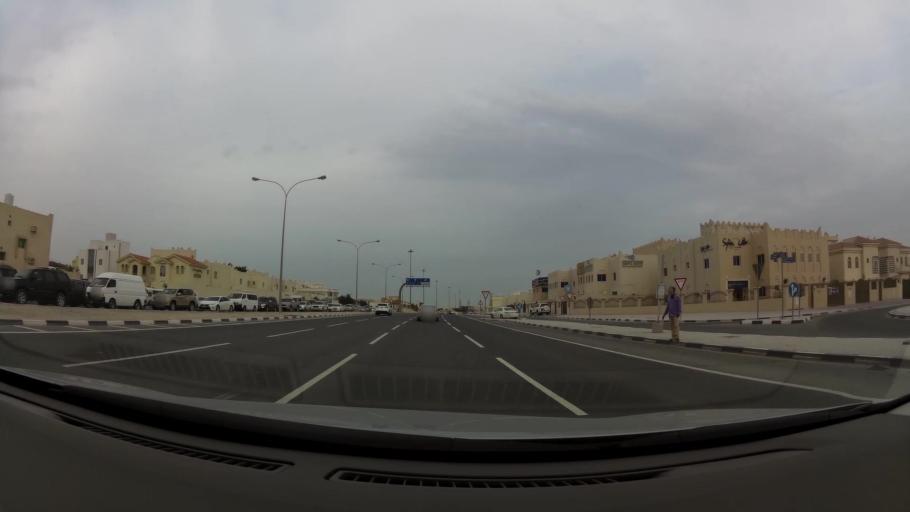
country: QA
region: Baladiyat ar Rayyan
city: Ar Rayyan
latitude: 25.3460
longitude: 51.4622
